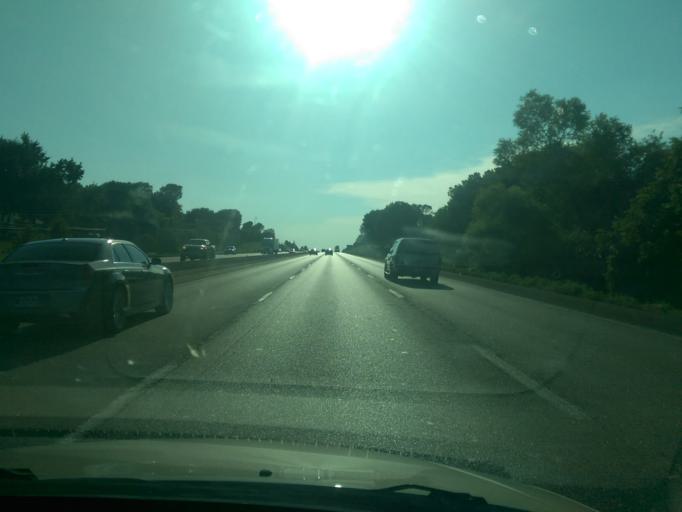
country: US
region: Missouri
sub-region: Jackson County
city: Independence
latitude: 39.0453
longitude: -94.3955
